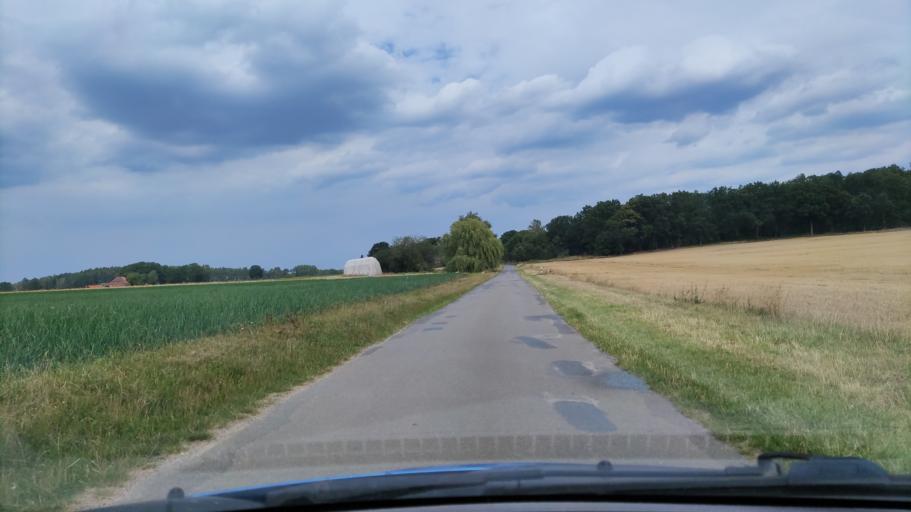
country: DE
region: Lower Saxony
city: Schnega
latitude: 52.9358
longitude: 10.8787
